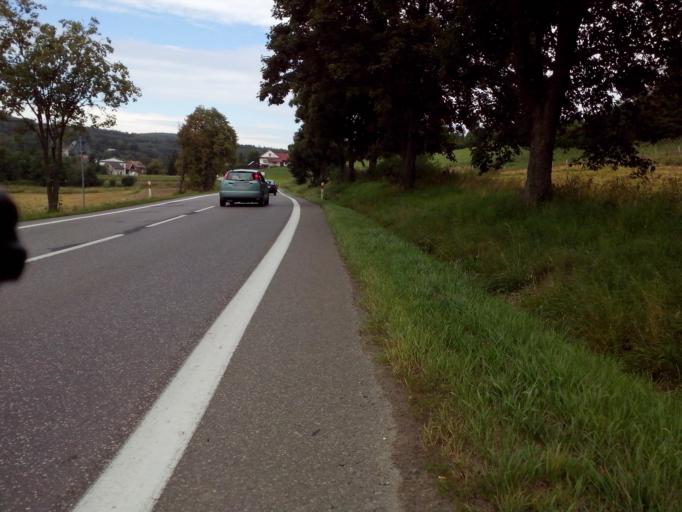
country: PL
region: Subcarpathian Voivodeship
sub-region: Powiat brzozowski
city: Domaradz
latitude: 49.7710
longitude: 21.9528
